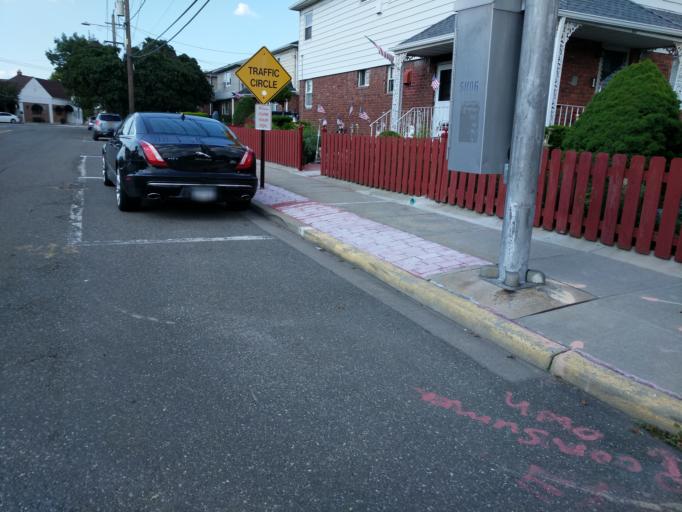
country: US
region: New York
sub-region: Nassau County
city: Hewlett
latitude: 40.6499
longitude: -73.7011
